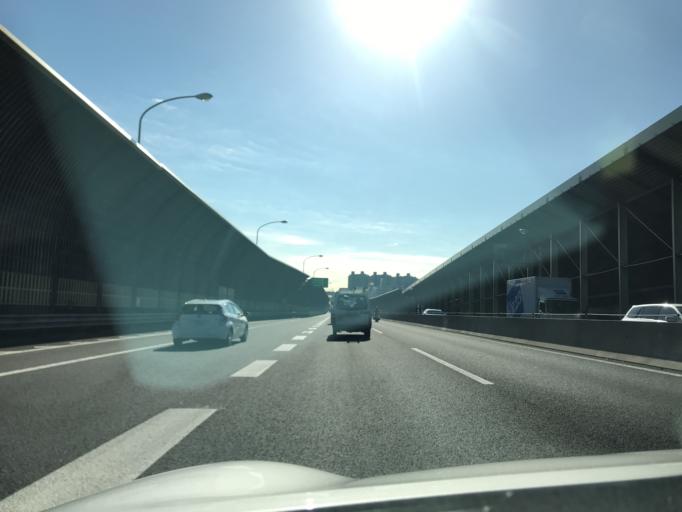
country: JP
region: Chiba
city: Chiba
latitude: 35.6356
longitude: 140.1217
